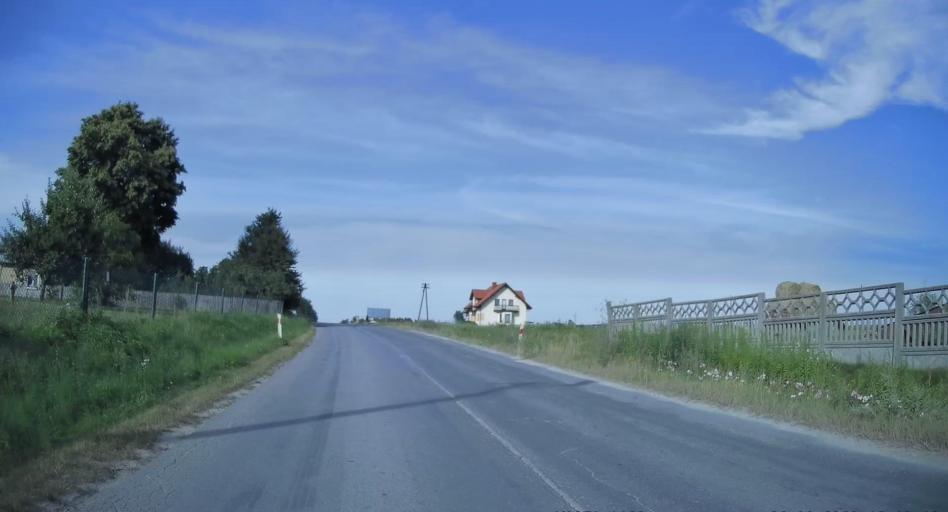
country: PL
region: Swietokrzyskie
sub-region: Powiat kielecki
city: Lopuszno
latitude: 50.9731
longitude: 20.2420
